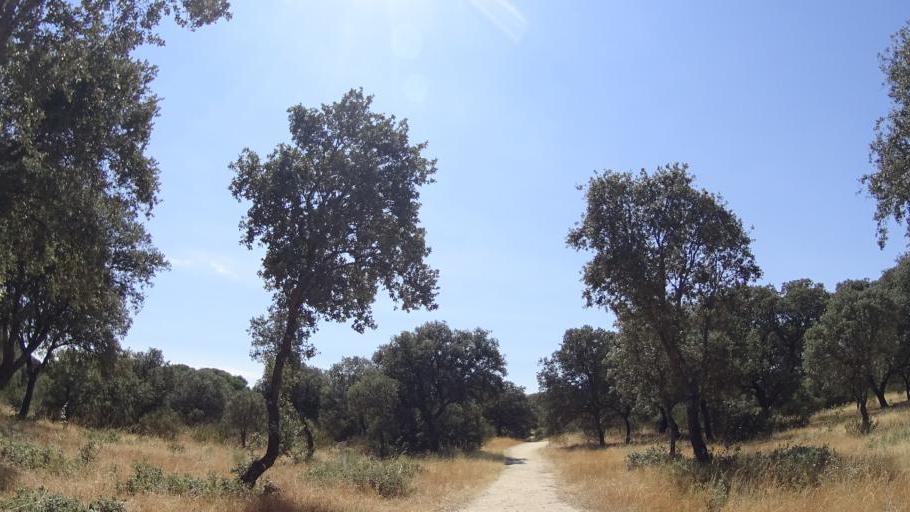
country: ES
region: Madrid
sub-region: Provincia de Madrid
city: Majadahonda
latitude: 40.4393
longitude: -3.8731
